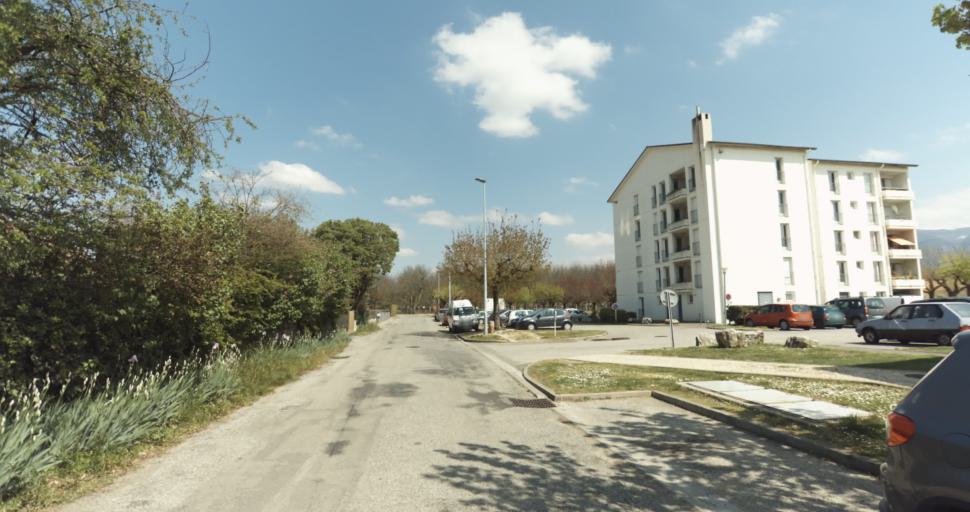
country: FR
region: Rhone-Alpes
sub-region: Departement de l'Isere
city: Saint-Marcellin
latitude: 45.1434
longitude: 5.3163
